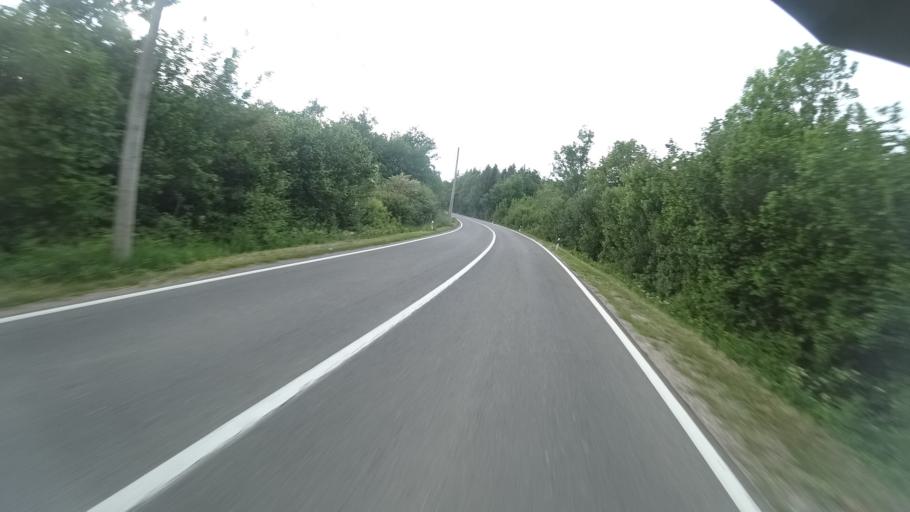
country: HR
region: Licko-Senjska
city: Gospic
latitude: 44.4945
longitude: 15.4599
